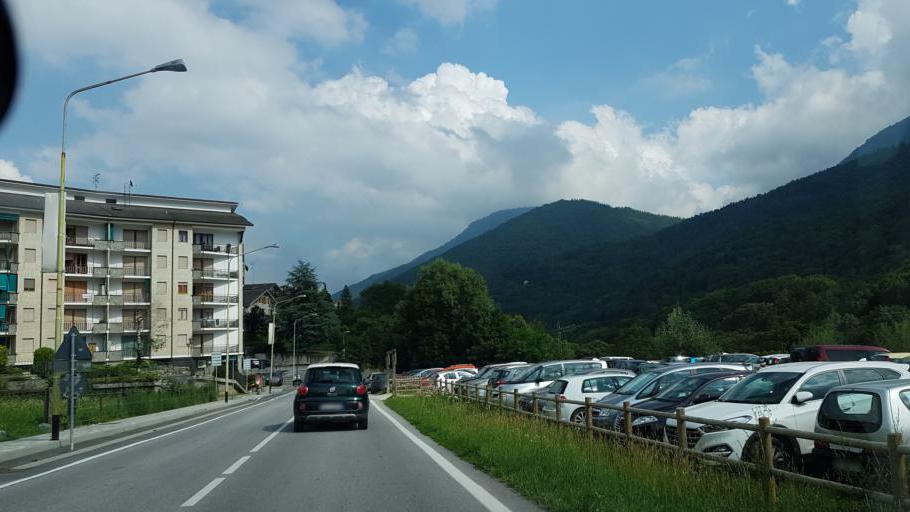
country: IT
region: Piedmont
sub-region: Provincia di Cuneo
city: Sampeyre
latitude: 44.5780
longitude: 7.1880
